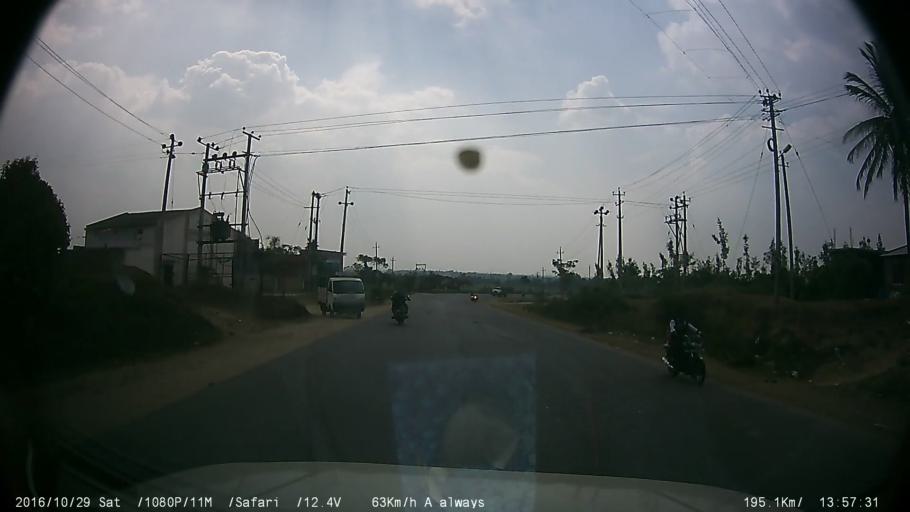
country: IN
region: Karnataka
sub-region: Mysore
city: Piriyapatna
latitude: 12.3354
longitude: 76.1547
